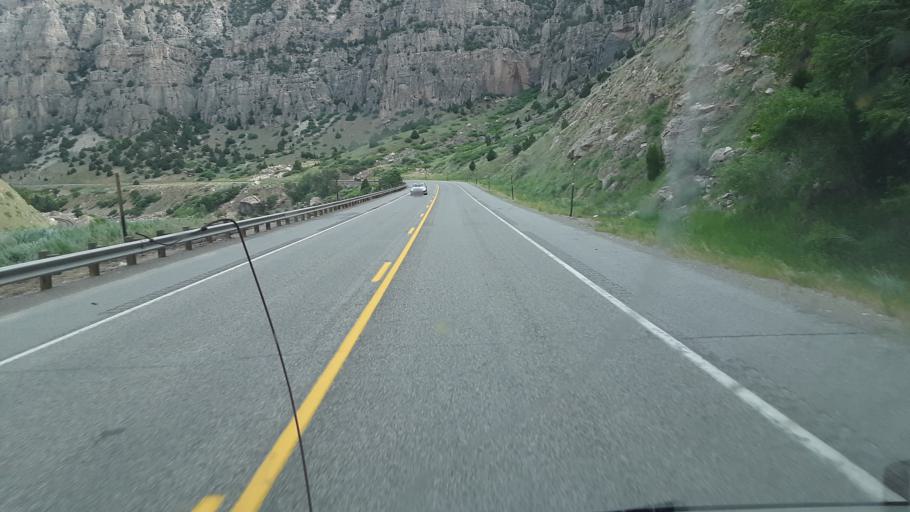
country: US
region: Wyoming
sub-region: Hot Springs County
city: Thermopolis
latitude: 43.5227
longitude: -108.1766
